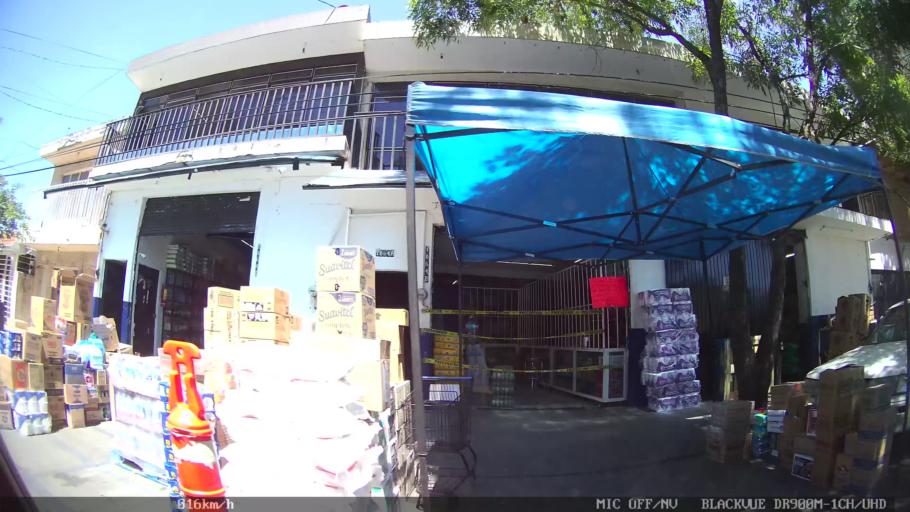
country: MX
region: Jalisco
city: Tlaquepaque
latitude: 20.6758
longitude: -103.2733
